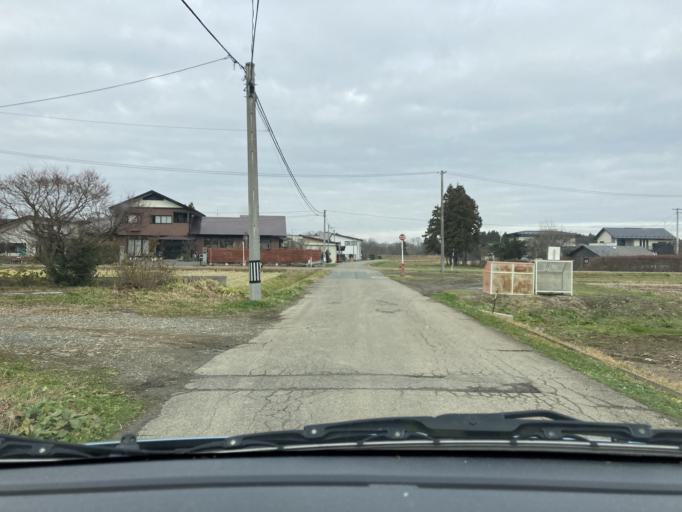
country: JP
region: Iwate
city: Kitakami
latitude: 39.2841
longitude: 141.0585
